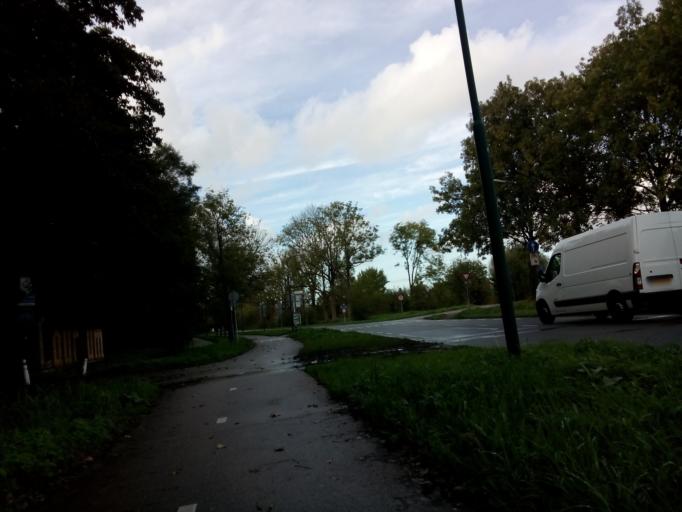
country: NL
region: Utrecht
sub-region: Gemeente Woerden
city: Woerden
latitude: 52.0914
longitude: 4.8936
